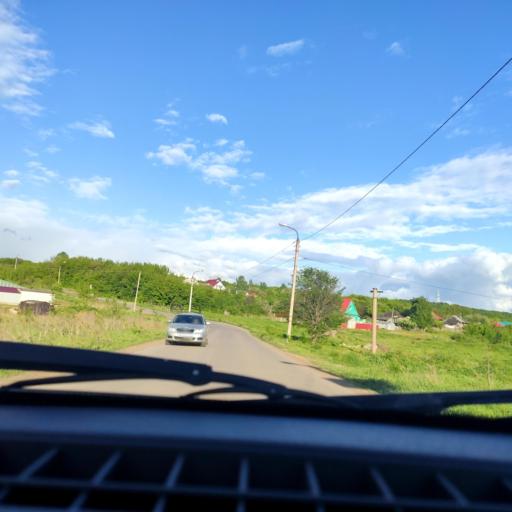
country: RU
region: Bashkortostan
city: Blagoveshchensk
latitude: 54.8892
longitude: 56.0365
